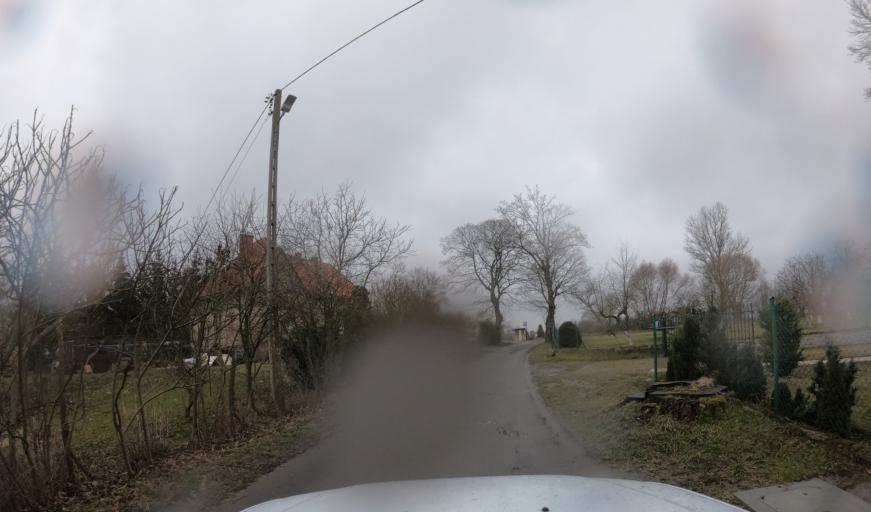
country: PL
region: West Pomeranian Voivodeship
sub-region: Powiat kamienski
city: Kamien Pomorski
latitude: 53.8938
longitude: 14.8270
